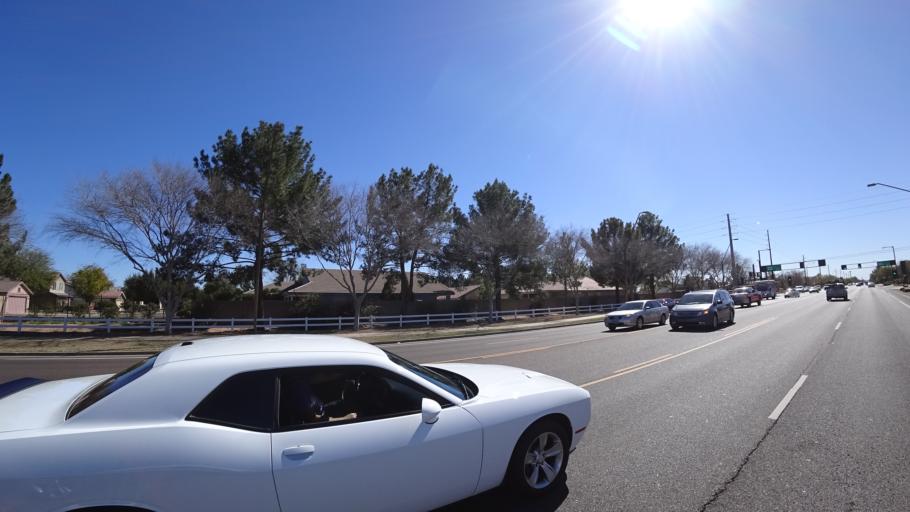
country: US
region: Arizona
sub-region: Maricopa County
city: Gilbert
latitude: 33.3511
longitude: -111.8072
